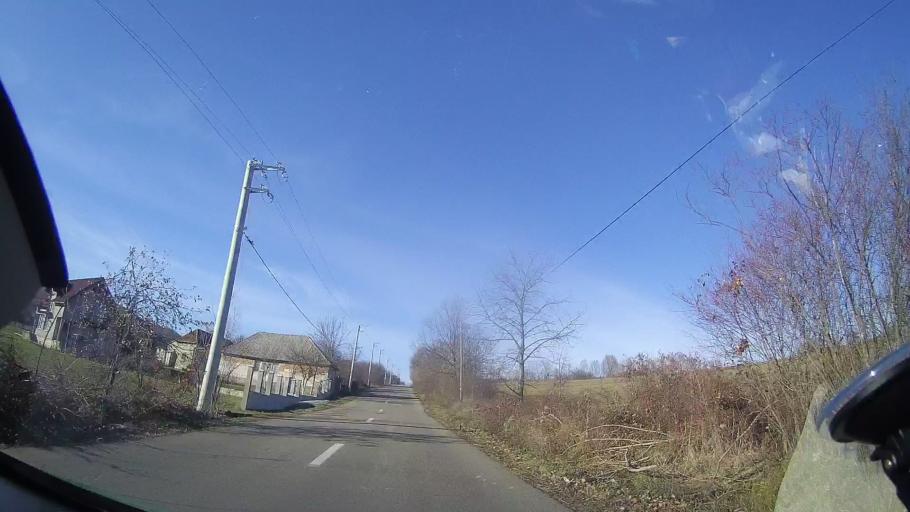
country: RO
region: Bihor
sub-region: Comuna Vadu Crisului
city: Vadu Crisului
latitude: 46.9727
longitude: 22.5431
